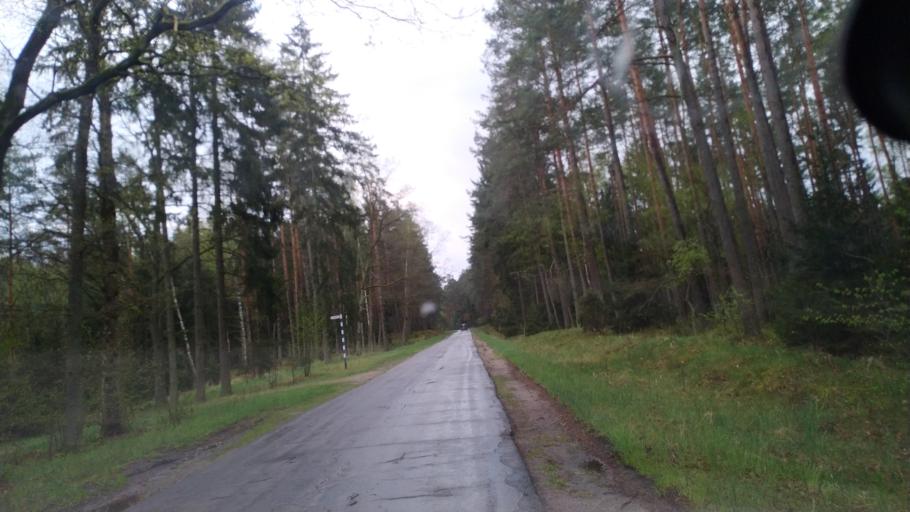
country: PL
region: Pomeranian Voivodeship
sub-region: Powiat starogardzki
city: Osiek
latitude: 53.6586
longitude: 18.4859
